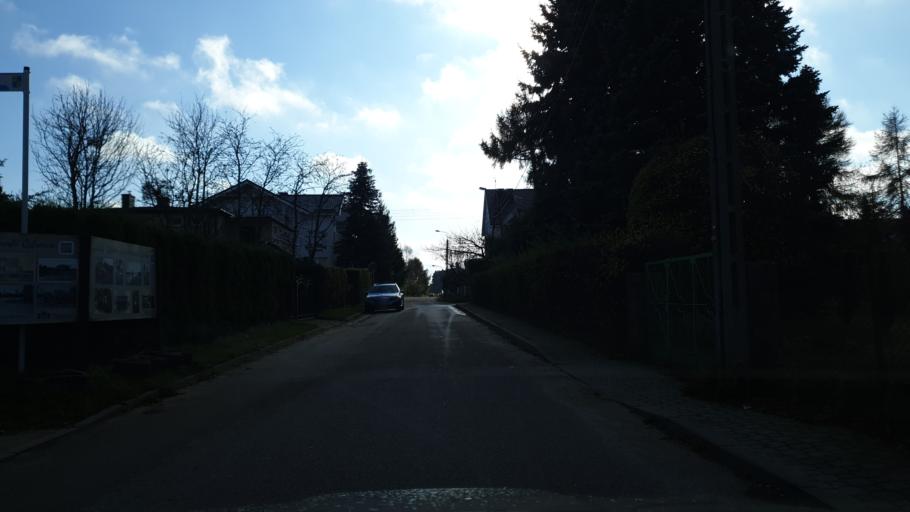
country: PL
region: Pomeranian Voivodeship
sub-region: Powiat pucki
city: Jastrzebia Gora
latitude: 54.8241
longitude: 18.2487
